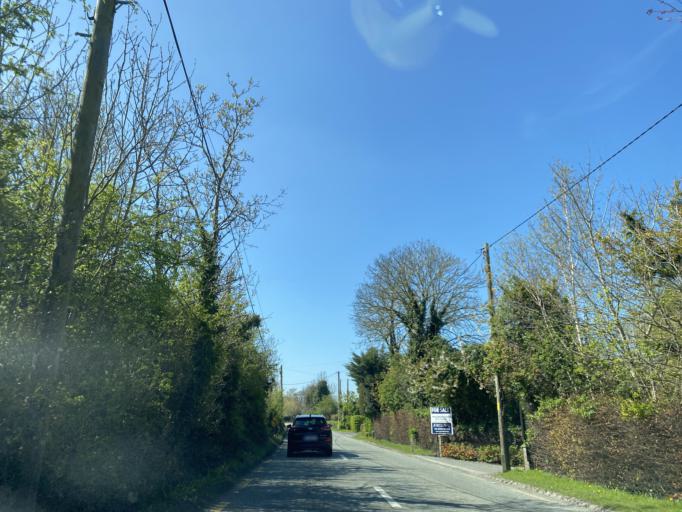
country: IE
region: Leinster
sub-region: Kildare
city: Kill
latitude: 53.2545
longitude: -6.5870
